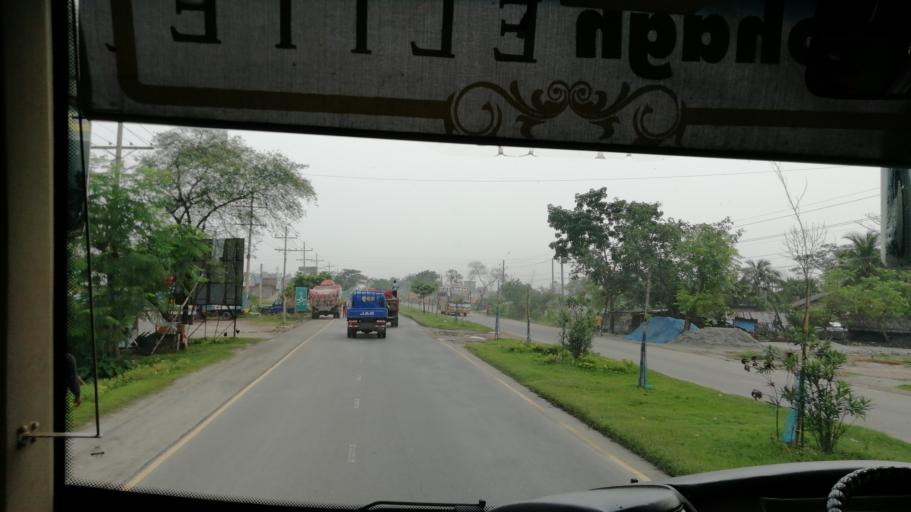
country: BD
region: Khulna
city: Khulna
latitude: 22.7953
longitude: 89.5302
